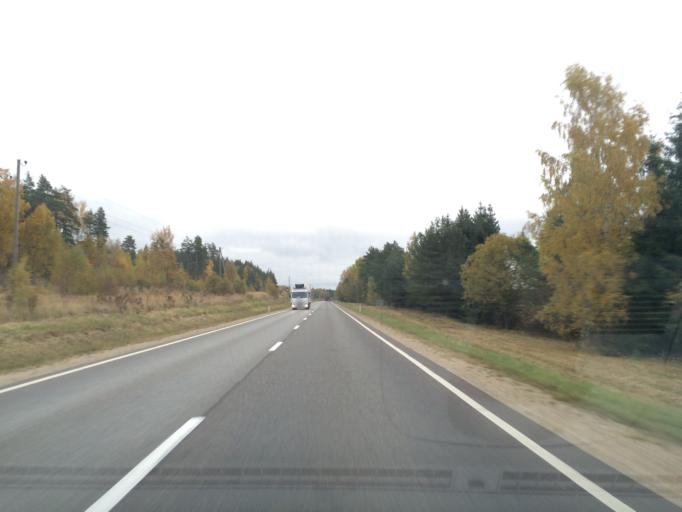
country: LV
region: Jekabpils Rajons
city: Jekabpils
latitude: 56.5357
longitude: 26.0410
